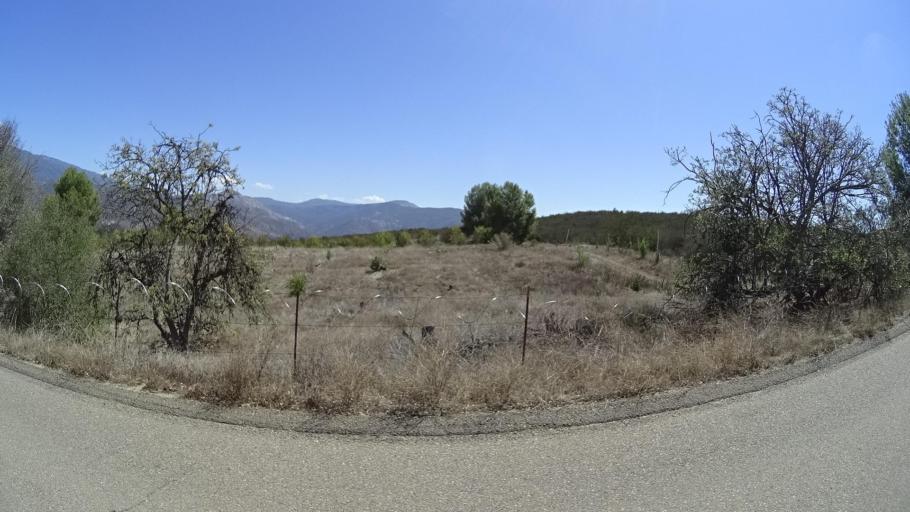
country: US
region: California
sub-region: San Diego County
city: Valley Center
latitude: 33.2869
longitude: -116.9859
